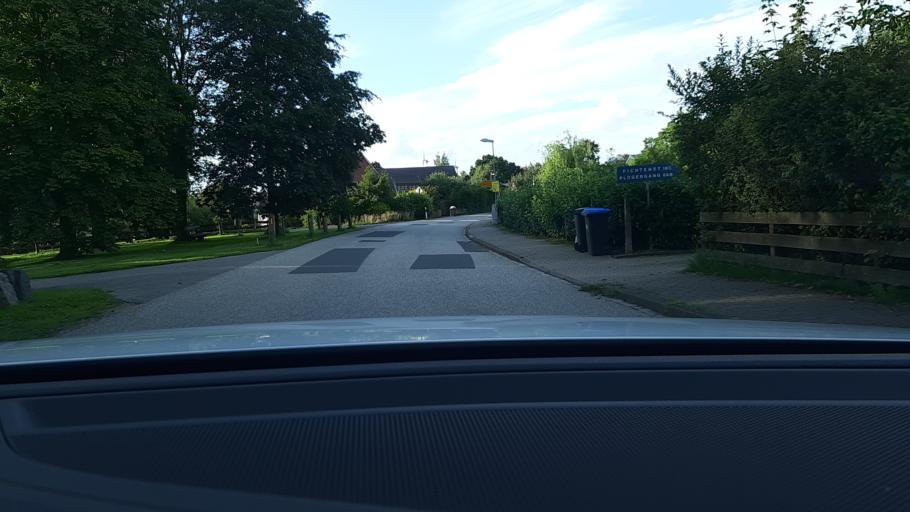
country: DE
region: Schleswig-Holstein
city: Monkhagen
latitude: 53.9178
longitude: 10.5506
